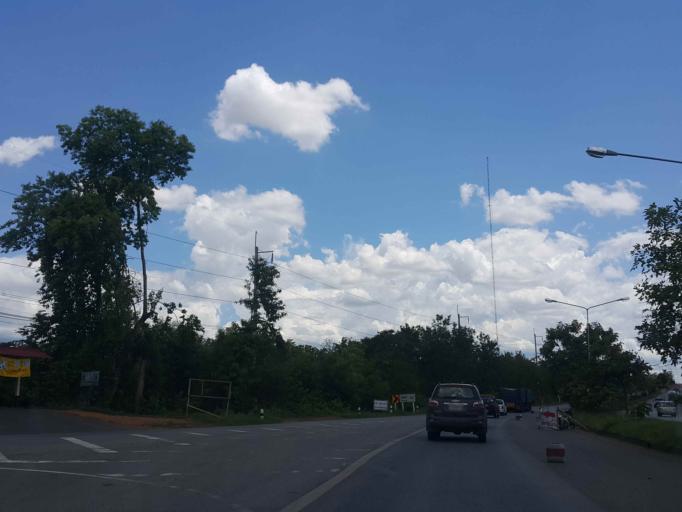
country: TH
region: Phrae
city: Nong Muang Khai
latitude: 18.2084
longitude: 100.1993
